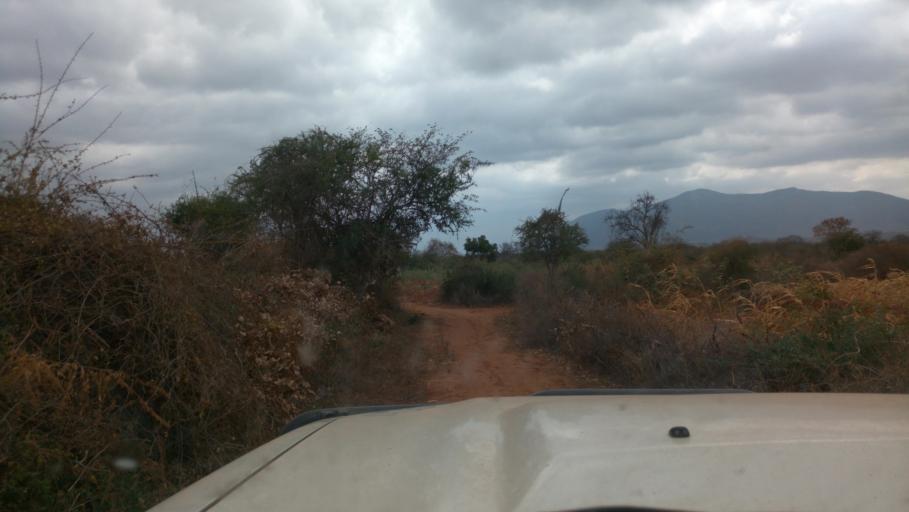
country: KE
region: Kitui
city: Kitui
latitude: -1.8547
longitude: 38.3518
